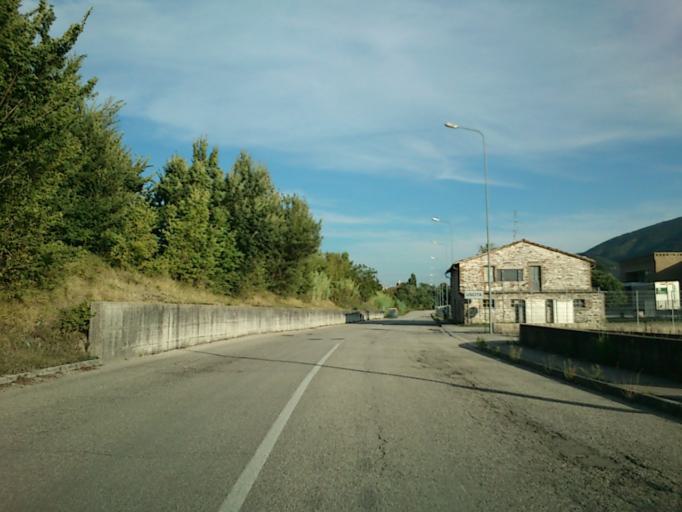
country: IT
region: The Marches
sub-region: Provincia di Pesaro e Urbino
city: Canavaccio
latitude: 43.6971
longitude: 12.6926
